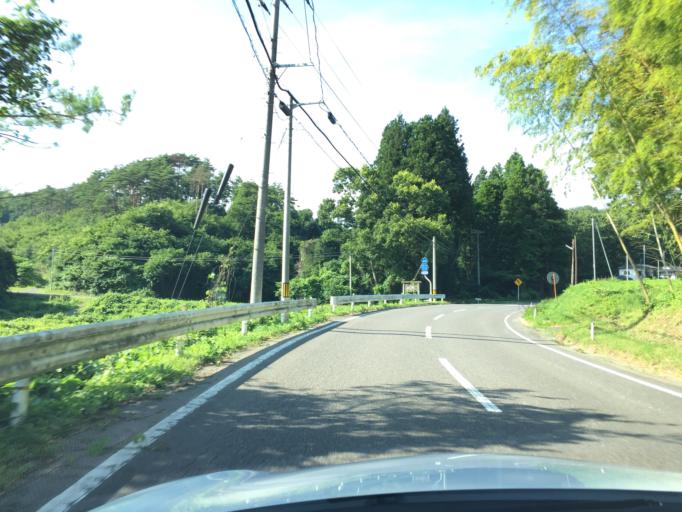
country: JP
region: Fukushima
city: Ishikawa
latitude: 37.2181
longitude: 140.4886
